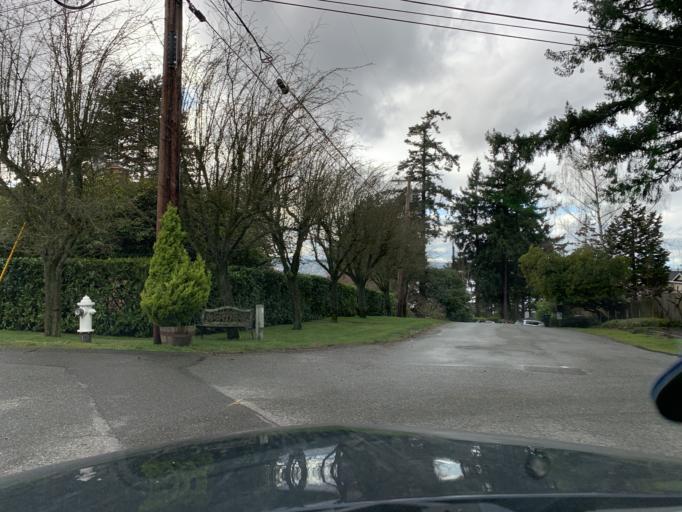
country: US
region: Washington
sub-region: King County
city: Mercer Island
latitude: 47.5844
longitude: -122.2441
